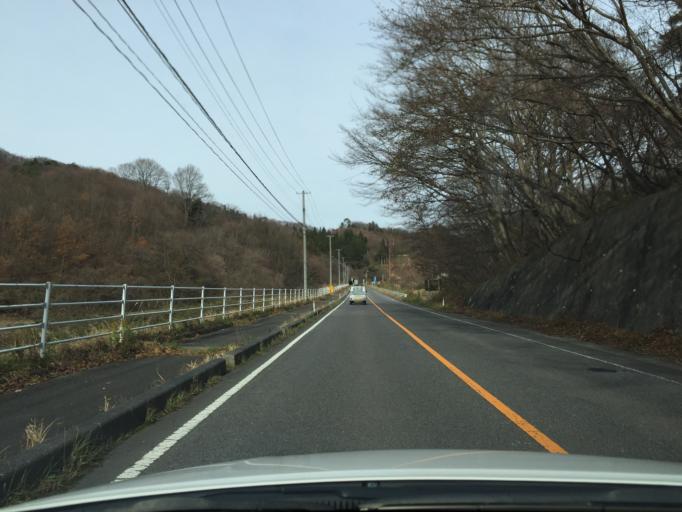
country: JP
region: Fukushima
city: Funehikimachi-funehiki
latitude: 37.3428
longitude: 140.6076
